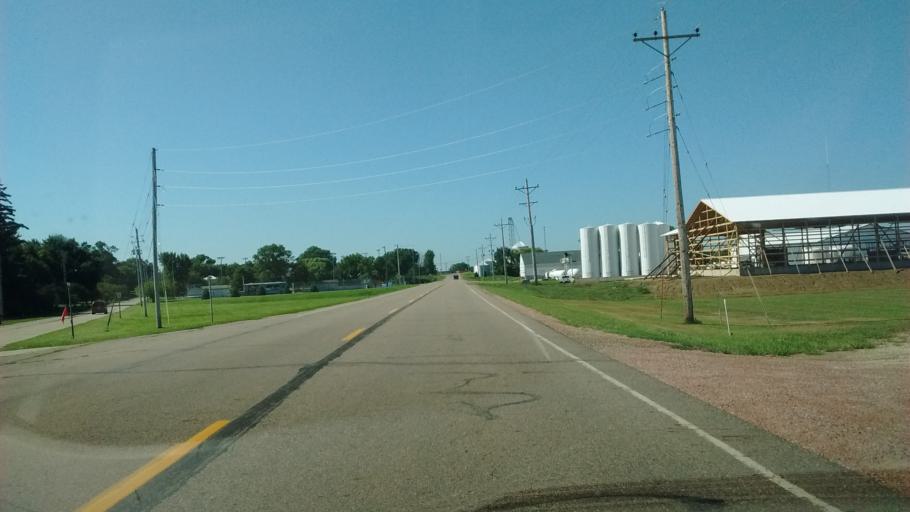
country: US
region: Iowa
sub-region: Woodbury County
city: Moville
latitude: 42.4945
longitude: -96.0725
